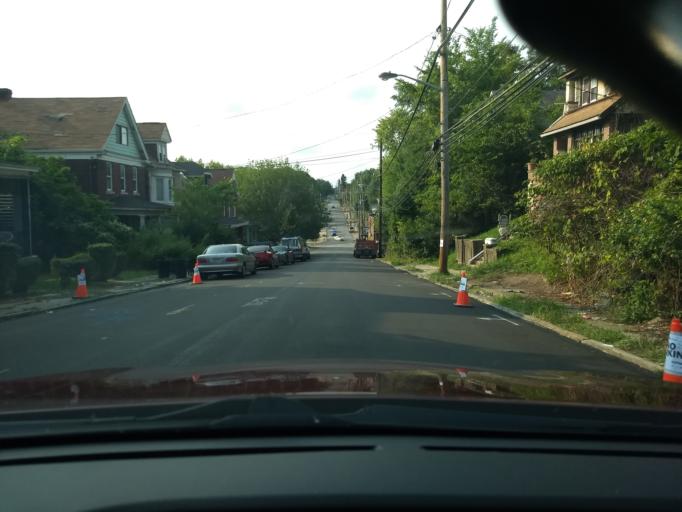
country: US
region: Pennsylvania
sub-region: Allegheny County
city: Aspinwall
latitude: 40.4676
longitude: -79.8952
